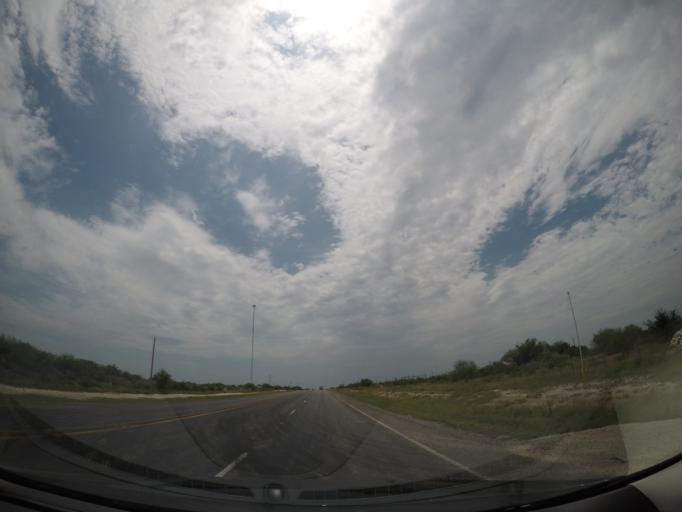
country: US
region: Texas
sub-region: Kinney County
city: Fort Clark Springs
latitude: 29.3441
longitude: -100.5655
